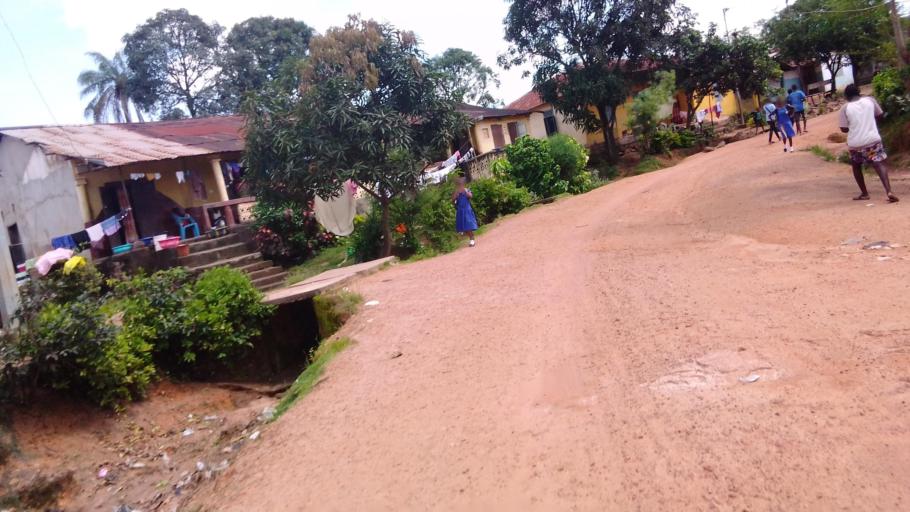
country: SL
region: Northern Province
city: Makeni
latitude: 8.8850
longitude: -12.0414
